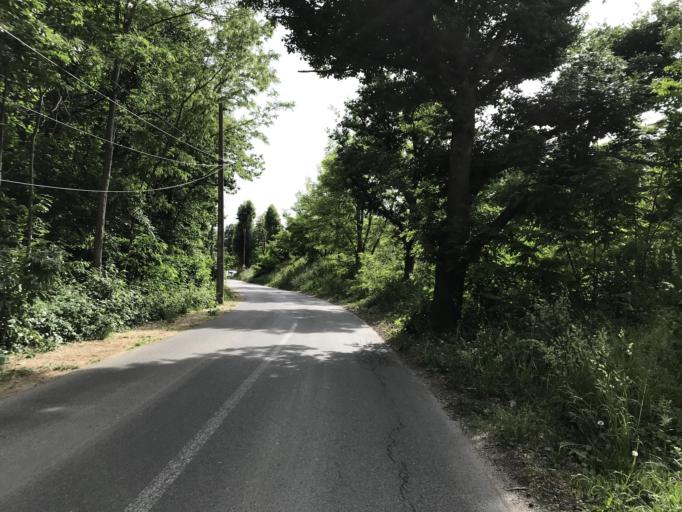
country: FR
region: Ile-de-France
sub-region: Departement de l'Essonne
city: La Ville-du-Bois
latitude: 48.6551
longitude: 2.2572
